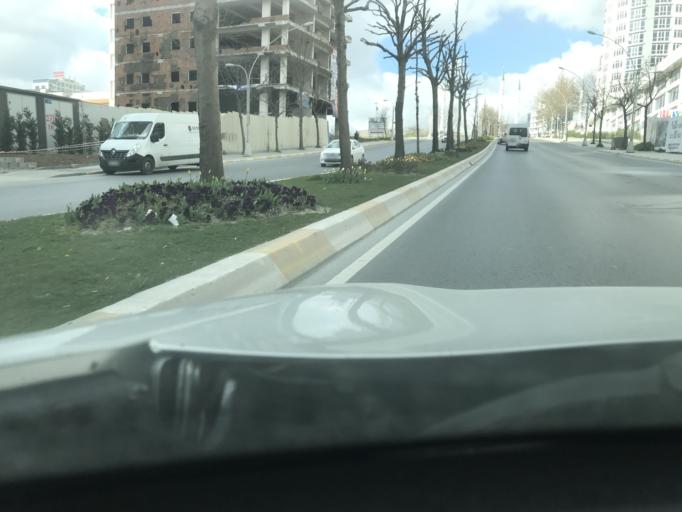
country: TR
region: Istanbul
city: Esenyurt
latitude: 41.0166
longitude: 28.6828
